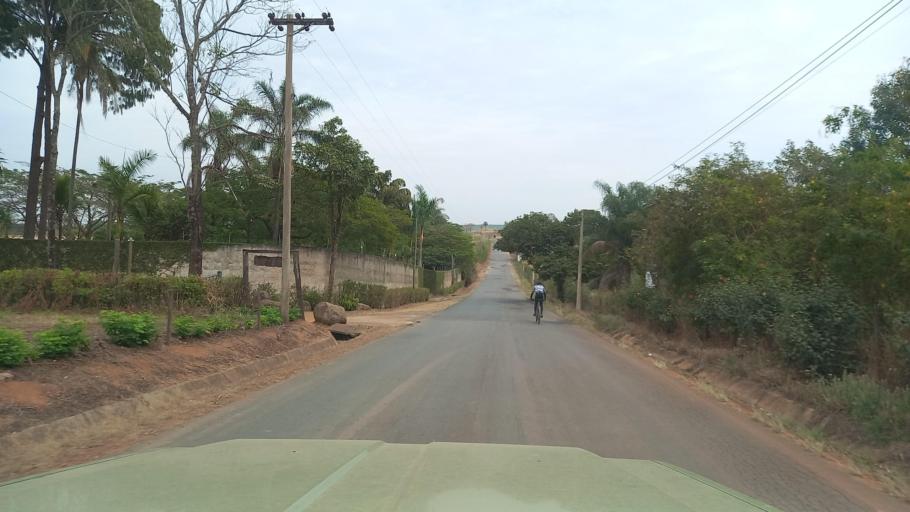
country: BR
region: Sao Paulo
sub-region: Moji-Guacu
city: Mogi-Gaucu
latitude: -22.3314
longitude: -46.8769
